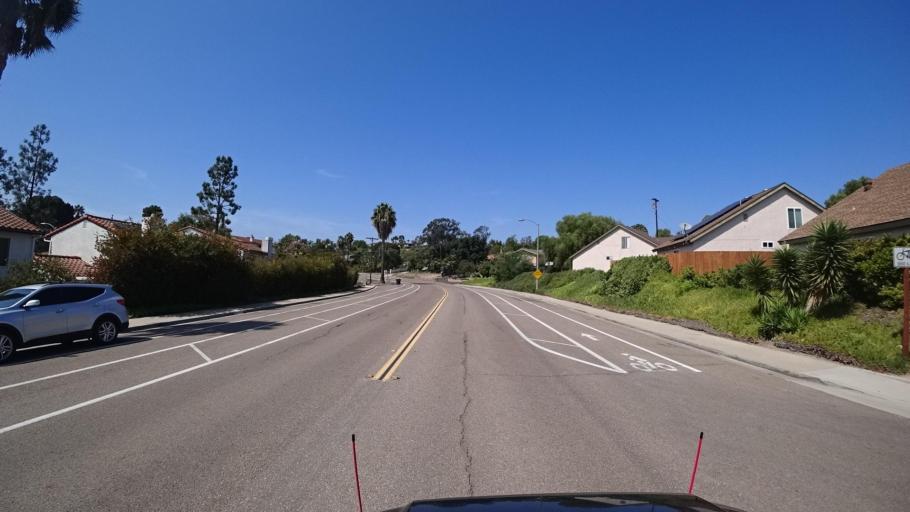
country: US
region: California
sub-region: San Diego County
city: Spring Valley
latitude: 32.7326
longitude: -116.9842
